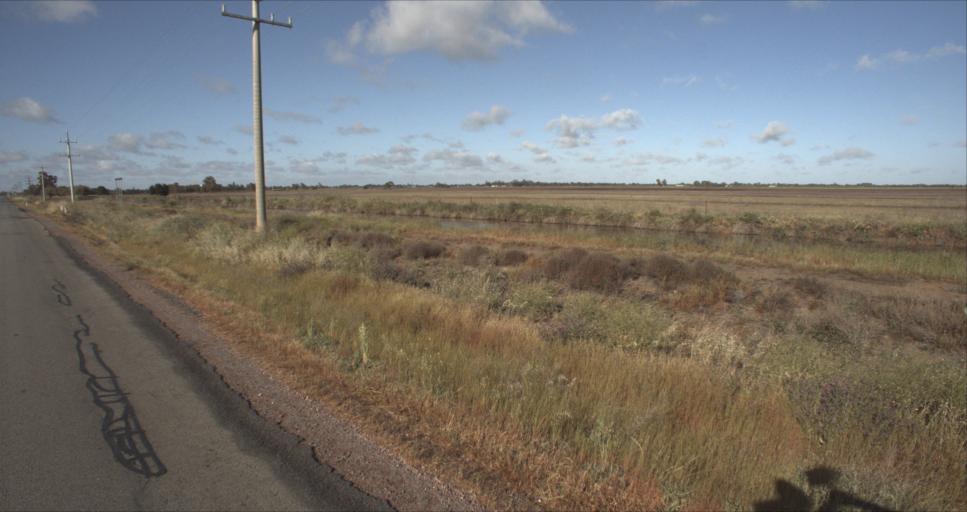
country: AU
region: New South Wales
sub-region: Leeton
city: Leeton
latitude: -34.5252
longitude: 146.3898
